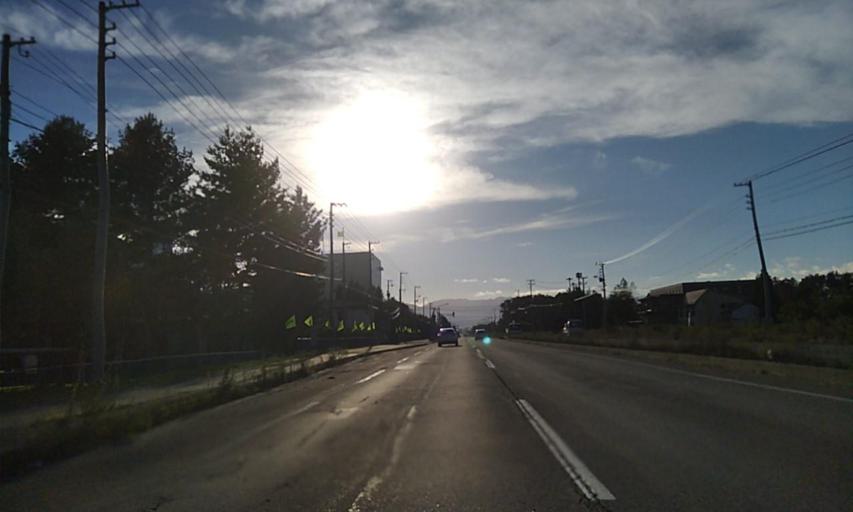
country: JP
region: Hokkaido
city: Obihiro
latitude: 42.9232
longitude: 143.0792
